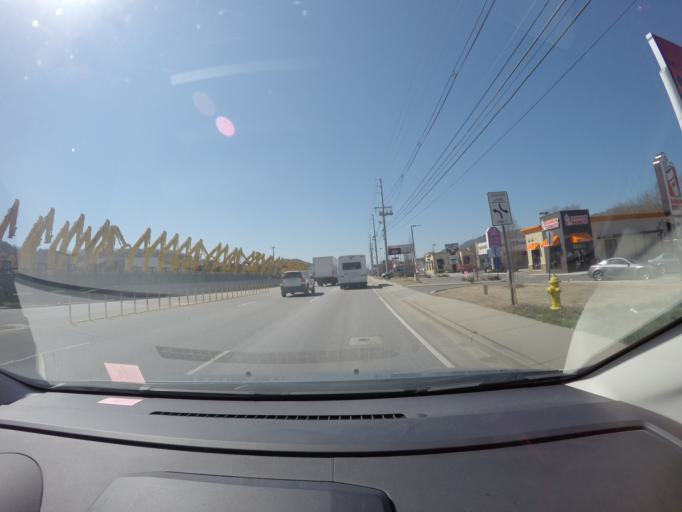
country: US
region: Tennessee
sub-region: Hamilton County
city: Signal Mountain
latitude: 35.0965
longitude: -85.3279
